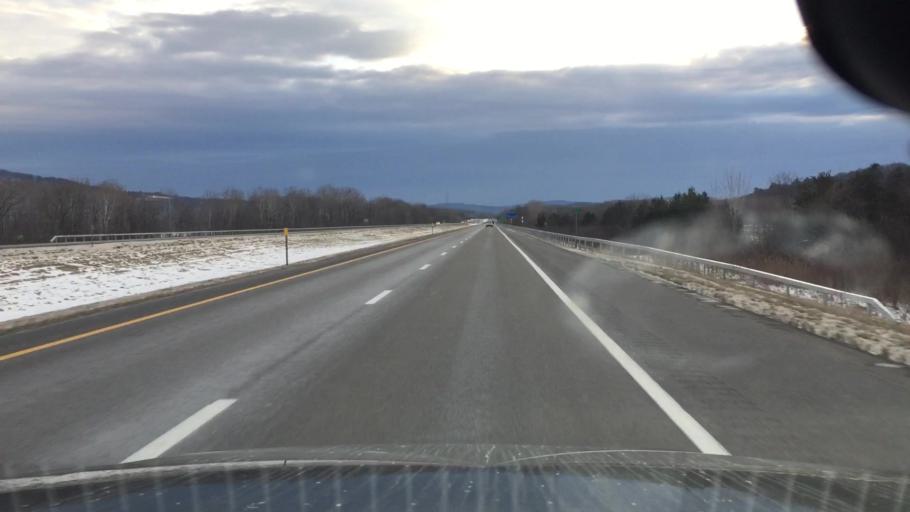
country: US
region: Pennsylvania
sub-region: Bradford County
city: South Waverly
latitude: 42.0009
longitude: -76.6069
